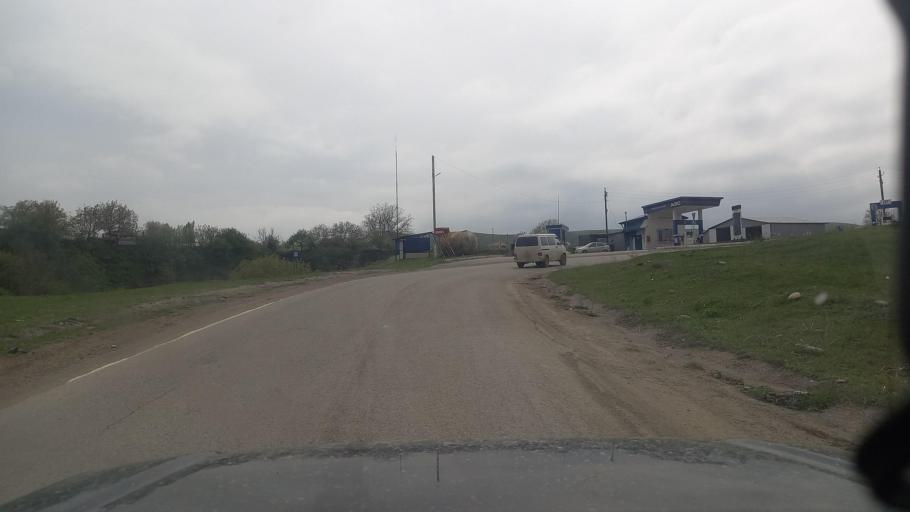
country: RU
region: Kabardino-Balkariya
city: Kamennomostskoye
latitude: 43.7336
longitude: 43.0479
